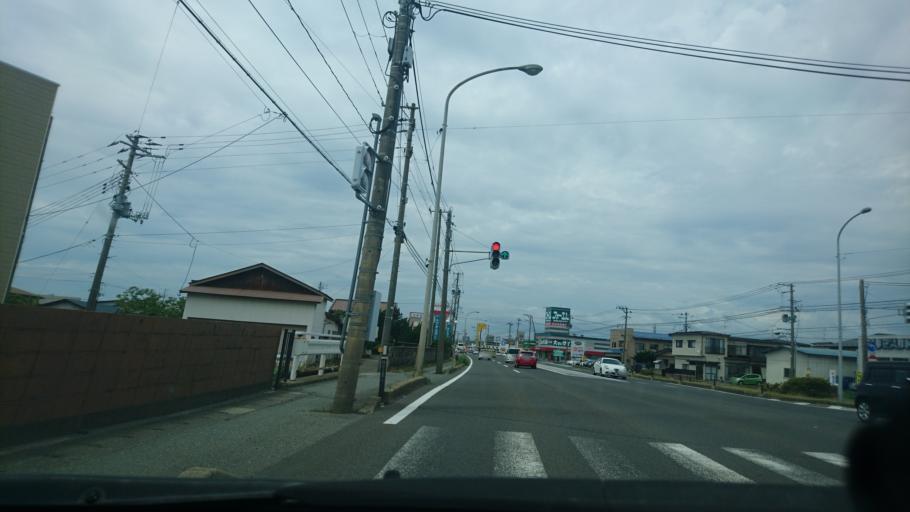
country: JP
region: Akita
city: Akita
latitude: 39.6836
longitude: 140.1256
